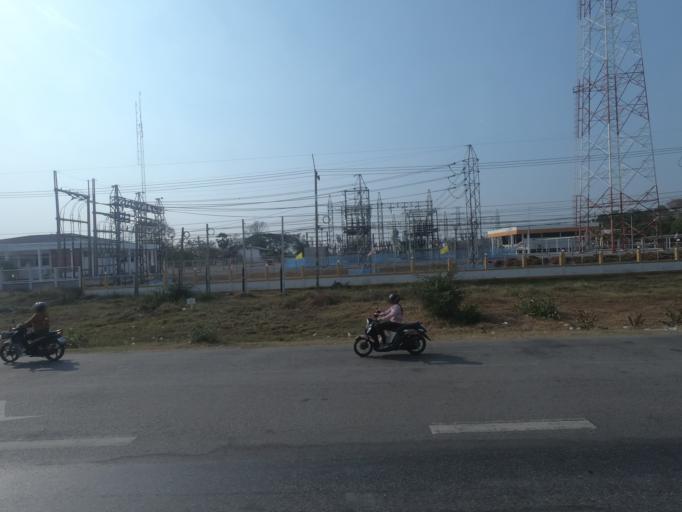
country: TH
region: Khon Kaen
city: Ban Phai
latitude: 16.0794
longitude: 102.7246
